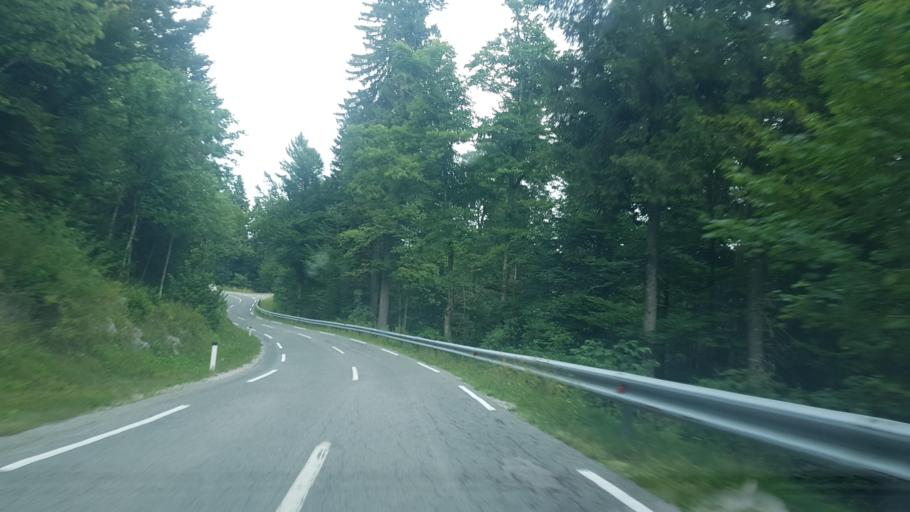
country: SI
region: Logatec
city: Logatec
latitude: 45.8759
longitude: 14.1449
